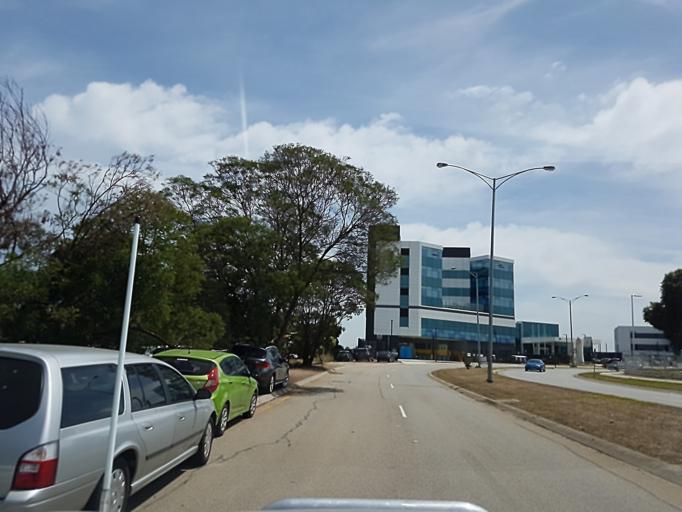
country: AU
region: Victoria
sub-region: Casey
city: Berwick
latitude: -38.0466
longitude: 145.3464
